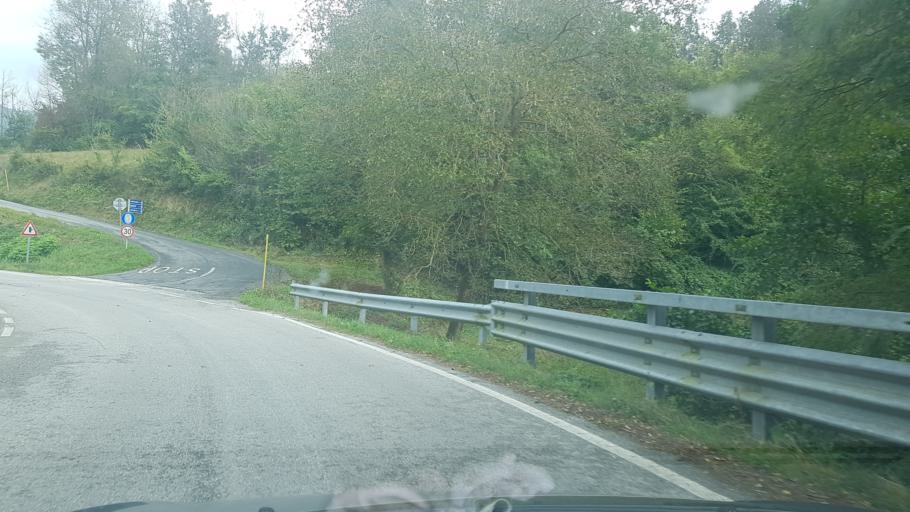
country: IT
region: Piedmont
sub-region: Provincia di Cuneo
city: Camerana
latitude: 44.4363
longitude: 8.1502
